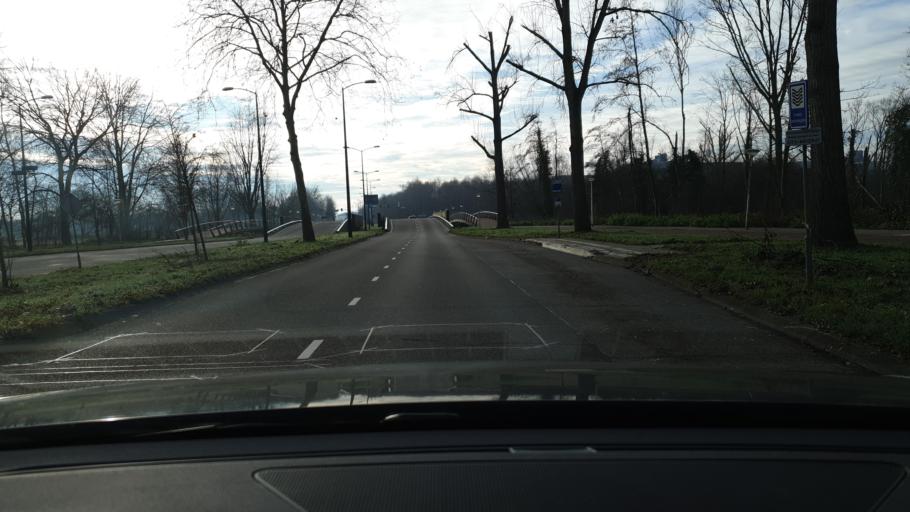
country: NL
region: North Brabant
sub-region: Gemeente Eindhoven
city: Eindhoven
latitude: 51.4169
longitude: 5.4651
